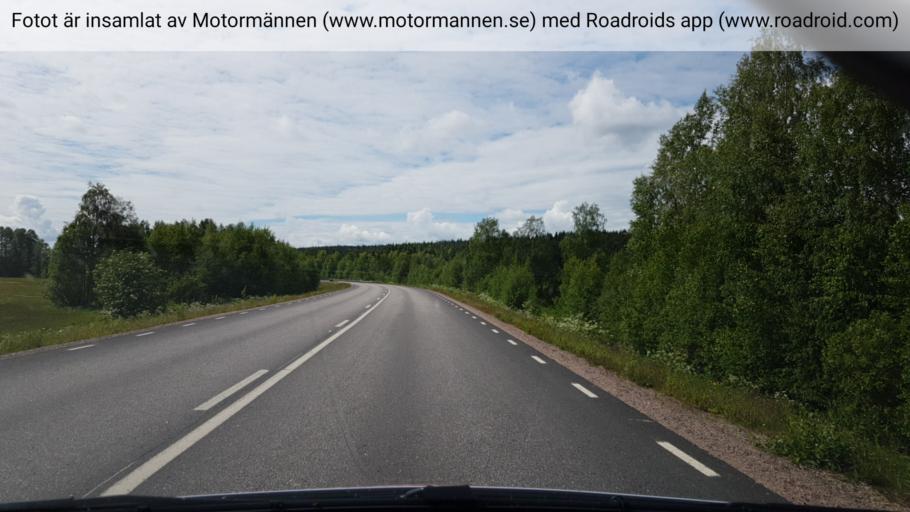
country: SE
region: Norrbotten
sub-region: Overtornea Kommun
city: OEvertornea
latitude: 66.4603
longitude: 23.6330
